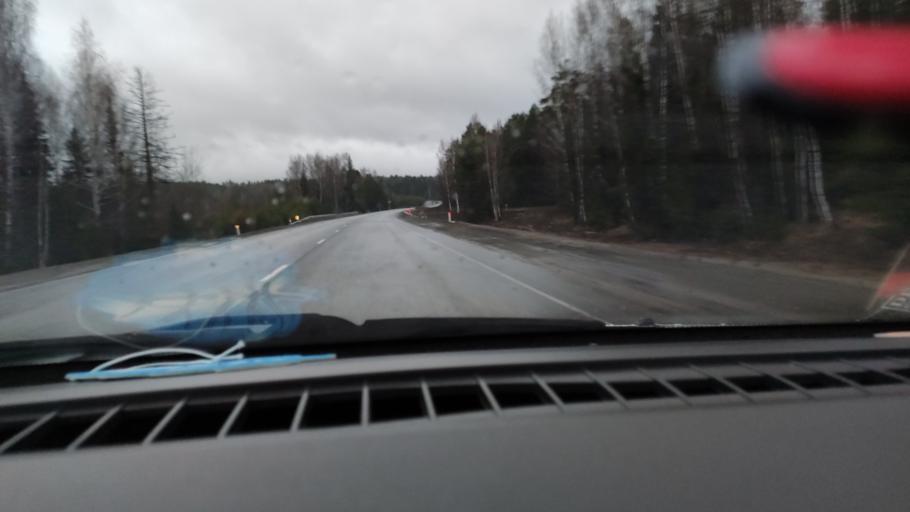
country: RU
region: Udmurtiya
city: Alnashi
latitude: 56.1026
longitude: 52.4579
